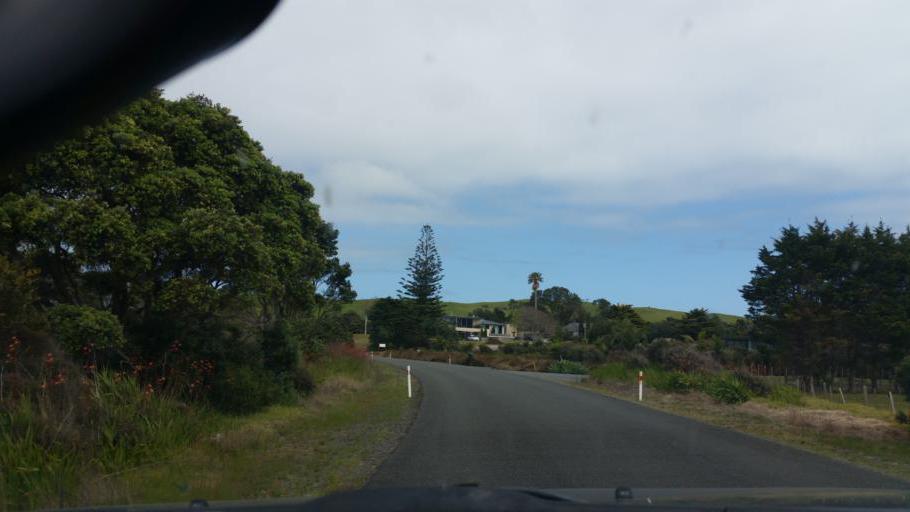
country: NZ
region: Northland
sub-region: Kaipara District
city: Dargaville
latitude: -35.8092
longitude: 173.6367
